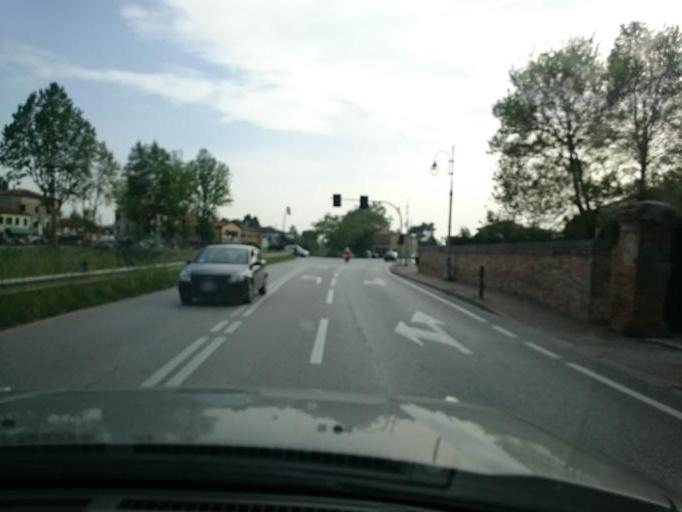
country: IT
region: Veneto
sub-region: Provincia di Venezia
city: Fornase
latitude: 45.4473
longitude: 12.1625
